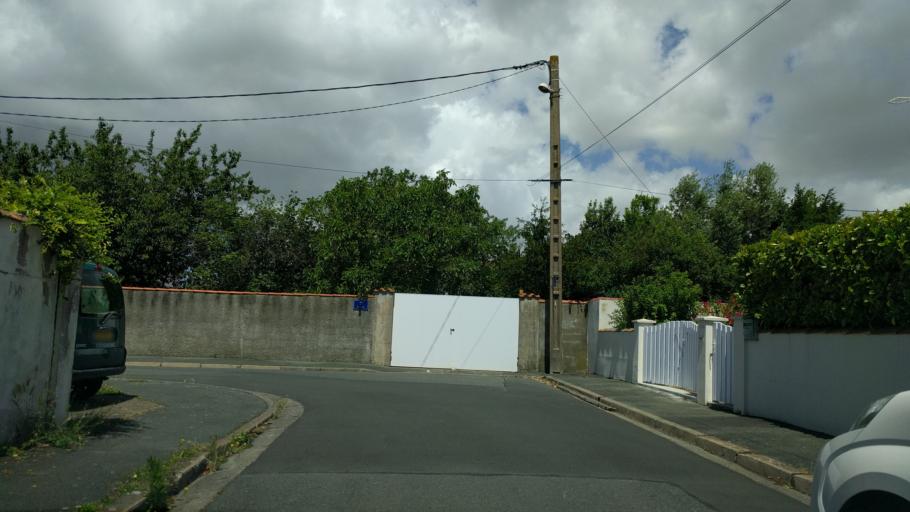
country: FR
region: Poitou-Charentes
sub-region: Departement de la Charente-Maritime
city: Puilboreau
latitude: 46.1683
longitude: -1.1288
